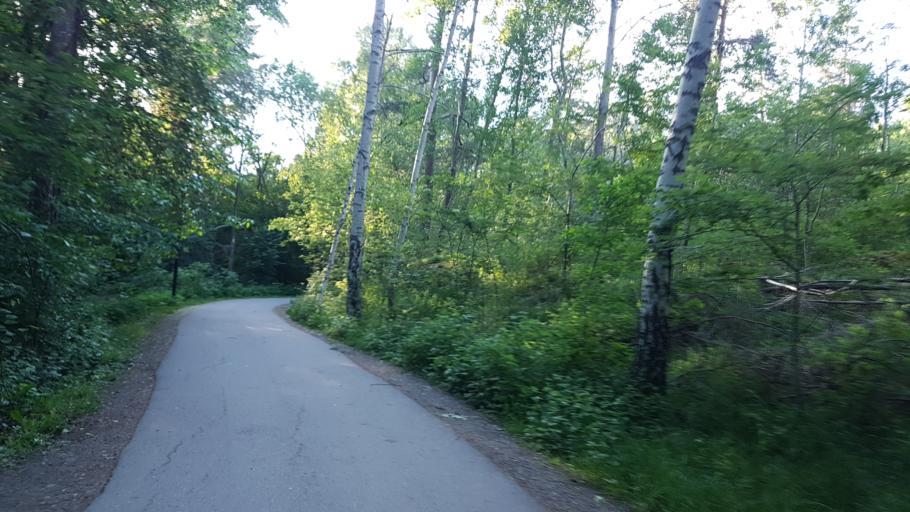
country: SE
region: Stockholm
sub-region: Nacka Kommun
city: Nacka
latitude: 59.2831
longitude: 18.1215
